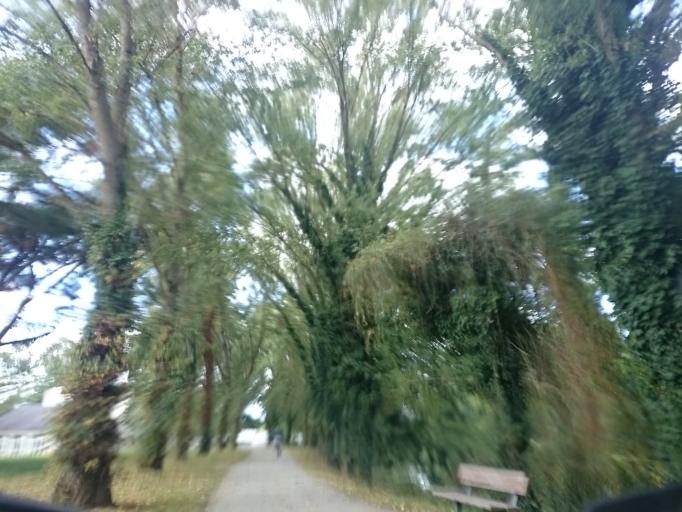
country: FR
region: Brittany
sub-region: Departement d'Ille-et-Vilaine
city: Cesson-Sevigne
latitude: 48.1231
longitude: -1.5897
